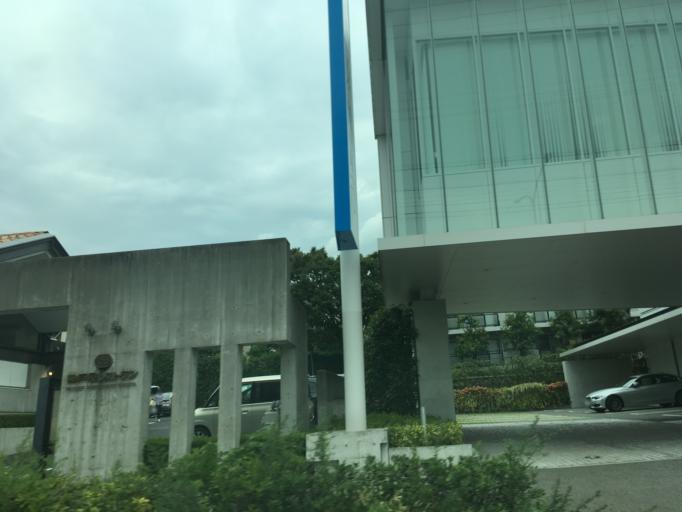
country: JP
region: Hyogo
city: Ashiya
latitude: 34.7230
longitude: 135.2601
